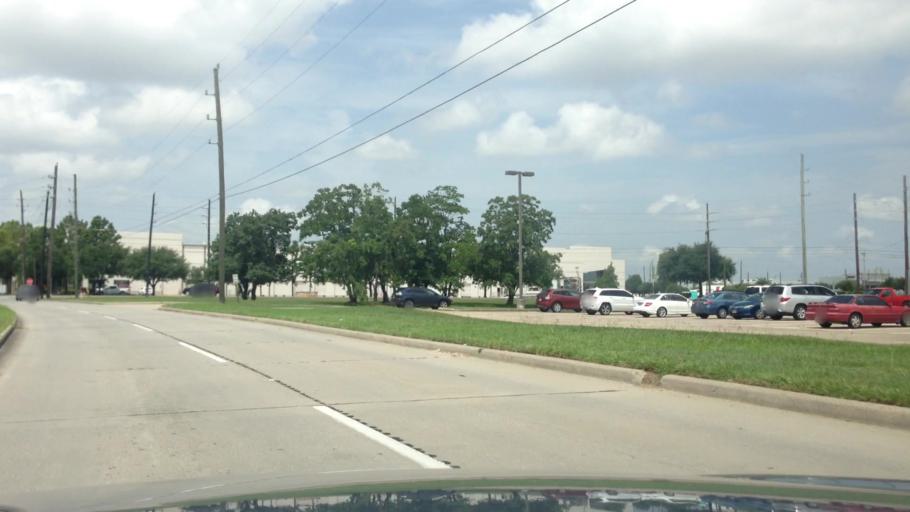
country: US
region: Texas
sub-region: Harris County
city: Jersey Village
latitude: 29.9266
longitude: -95.5466
